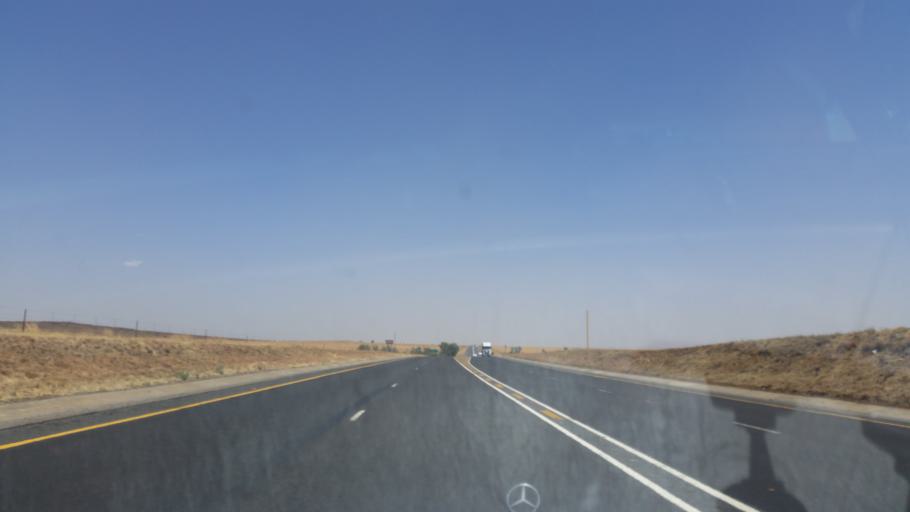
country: ZA
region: Orange Free State
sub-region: Lejweleputswa District Municipality
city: Brandfort
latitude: -28.8140
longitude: 26.6705
